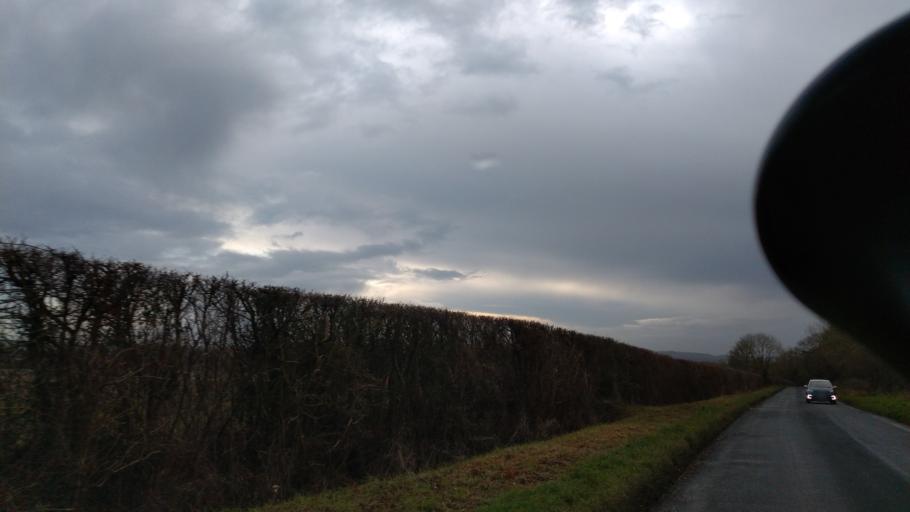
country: GB
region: England
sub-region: Borough of Swindon
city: Highworth
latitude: 51.6041
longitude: -1.7280
